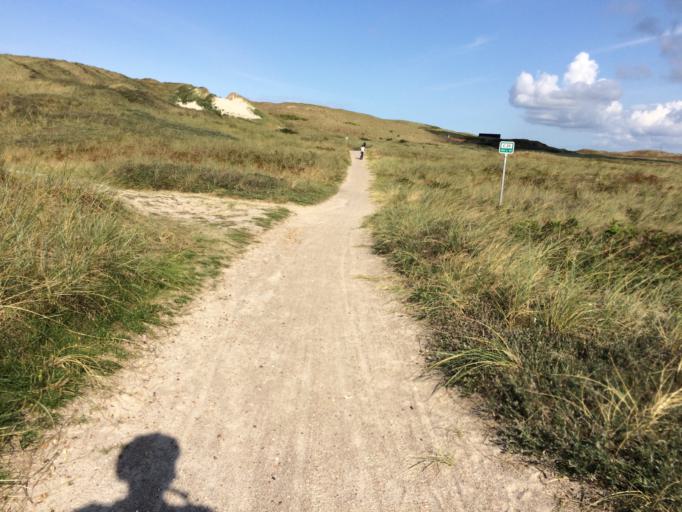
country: DK
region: Central Jutland
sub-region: Ringkobing-Skjern Kommune
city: Hvide Sande
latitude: 55.9311
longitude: 8.1507
